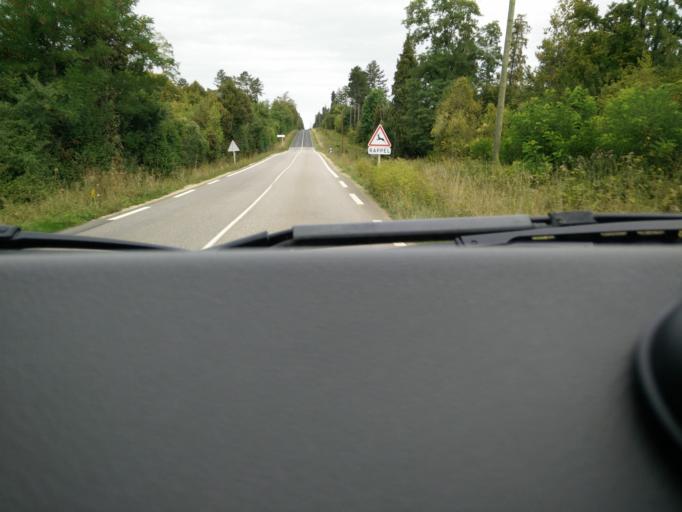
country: FR
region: Lorraine
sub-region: Departement de Meurthe-et-Moselle
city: Montauville
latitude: 48.9111
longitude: 5.9269
